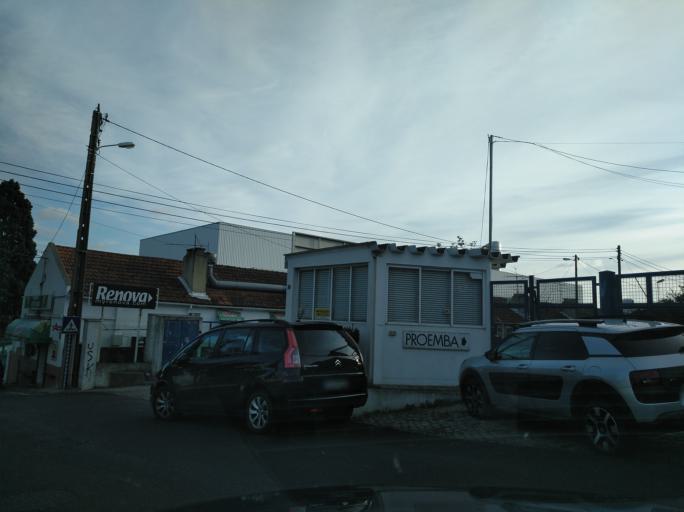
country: PT
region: Lisbon
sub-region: Oeiras
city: Alges
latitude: 38.7200
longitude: -9.2197
